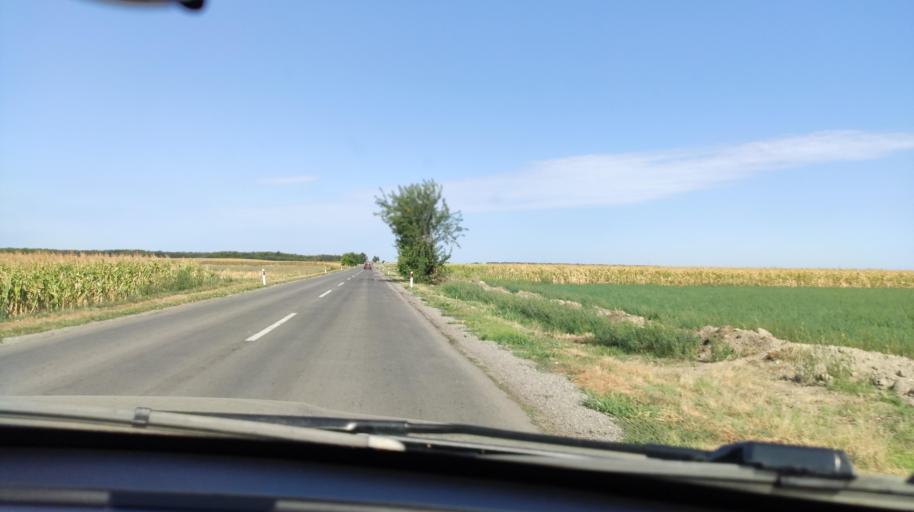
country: RS
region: Autonomna Pokrajina Vojvodina
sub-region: Severnobacki Okrug
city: Backa Topola
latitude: 45.8314
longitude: 19.5910
